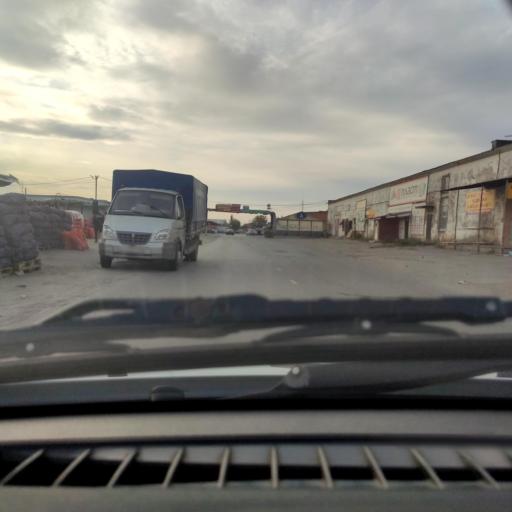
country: RU
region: Samara
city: Zhigulevsk
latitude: 53.5189
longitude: 49.4811
